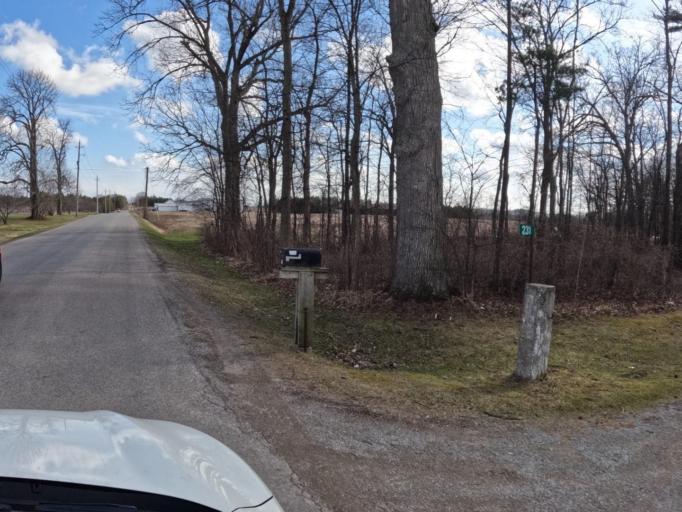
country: CA
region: Ontario
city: Norfolk County
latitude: 42.8667
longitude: -80.2762
